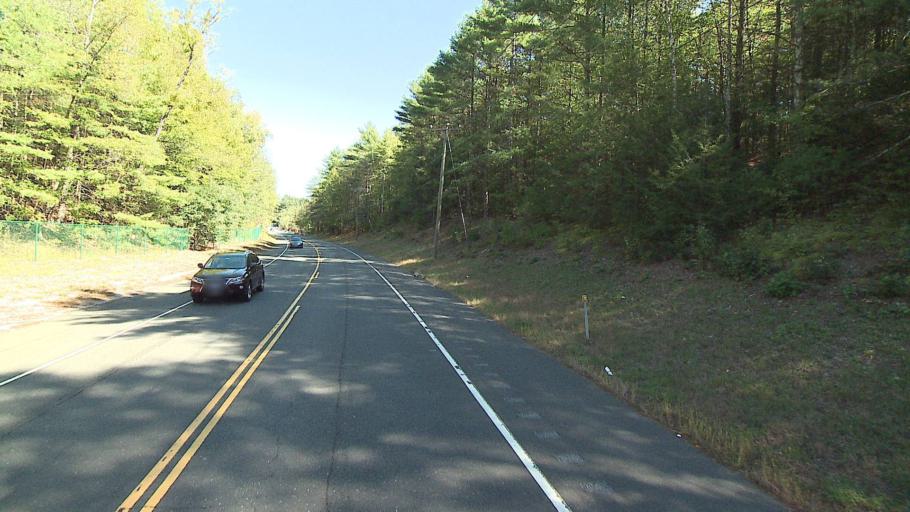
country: US
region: Connecticut
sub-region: Hartford County
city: Collinsville
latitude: 41.8209
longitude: -72.9535
